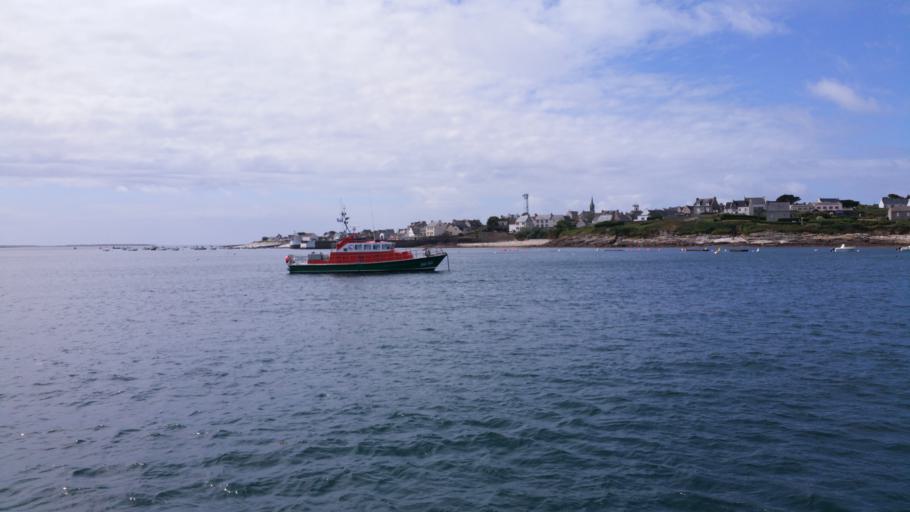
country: FR
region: Brittany
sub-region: Departement du Finistere
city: Le Conquet
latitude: 48.4016
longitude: -4.9548
